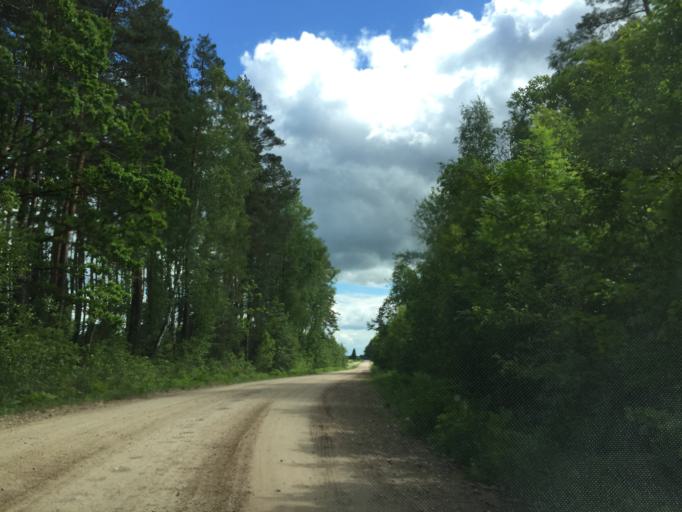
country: LV
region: Vecumnieki
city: Vecumnieki
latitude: 56.4858
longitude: 24.4129
